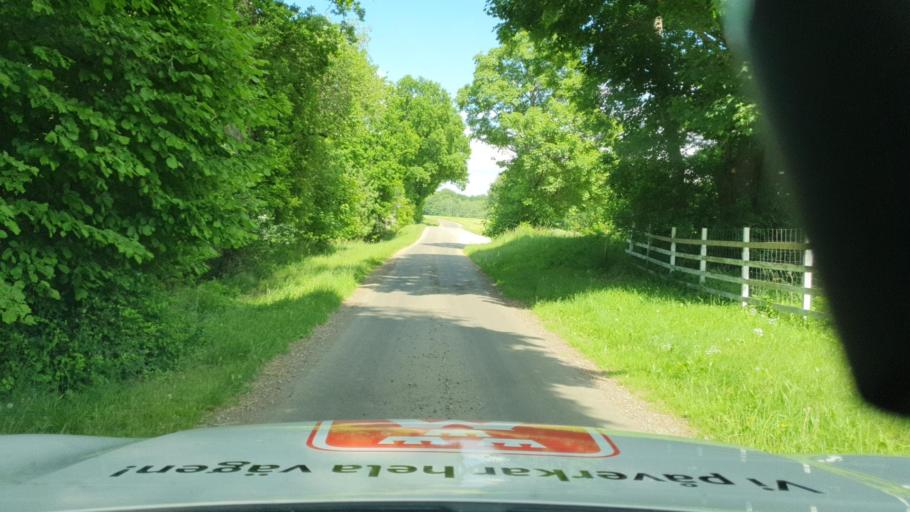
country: SE
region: Skane
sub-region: Lunds Kommun
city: Genarp
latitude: 55.5601
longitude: 13.4014
